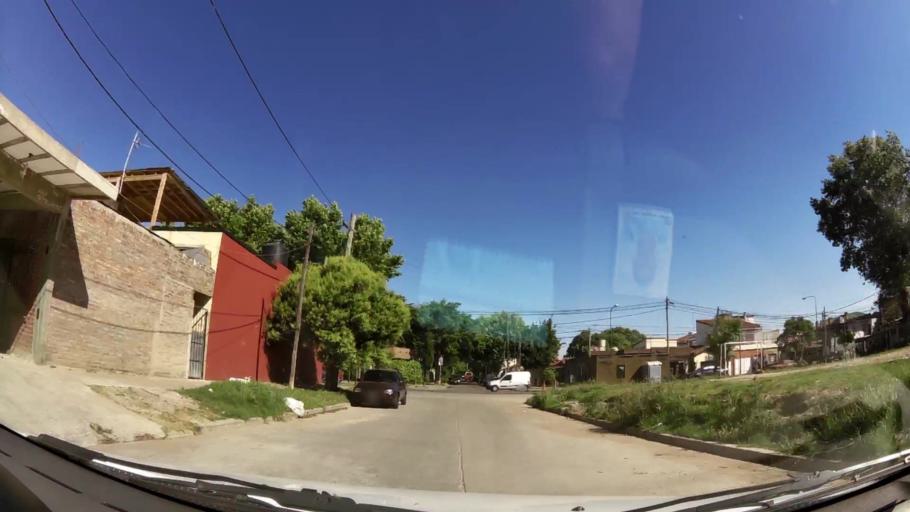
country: AR
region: Buenos Aires
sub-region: Partido de San Isidro
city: San Isidro
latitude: -34.4728
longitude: -58.5389
